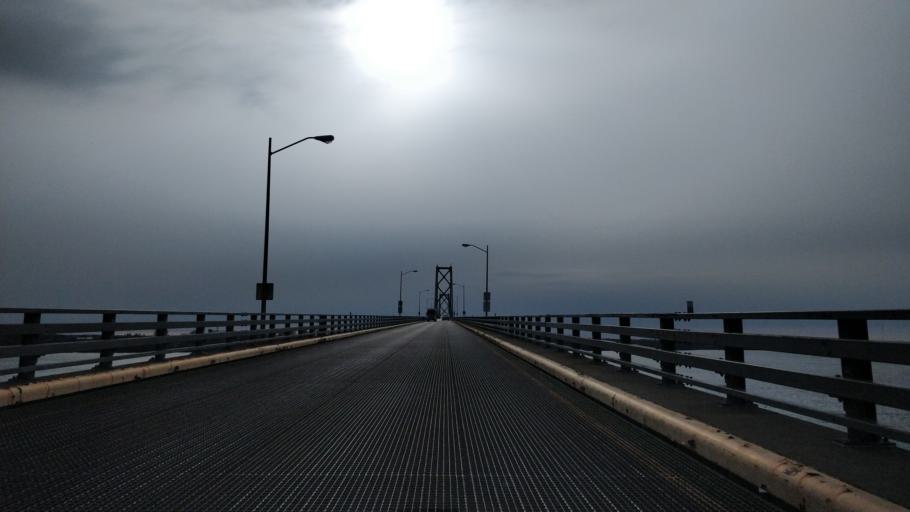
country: US
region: New York
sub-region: St. Lawrence County
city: Ogdensburg
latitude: 44.7412
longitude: -75.4641
